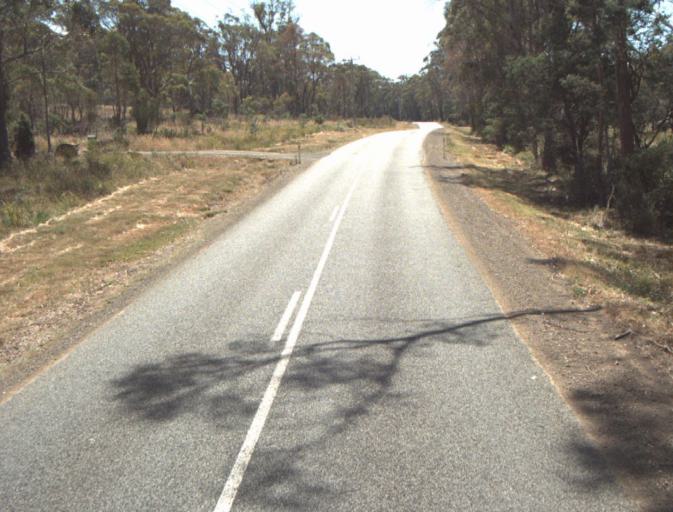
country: AU
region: Tasmania
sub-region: Launceston
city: Mayfield
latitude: -41.3323
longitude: 147.1408
